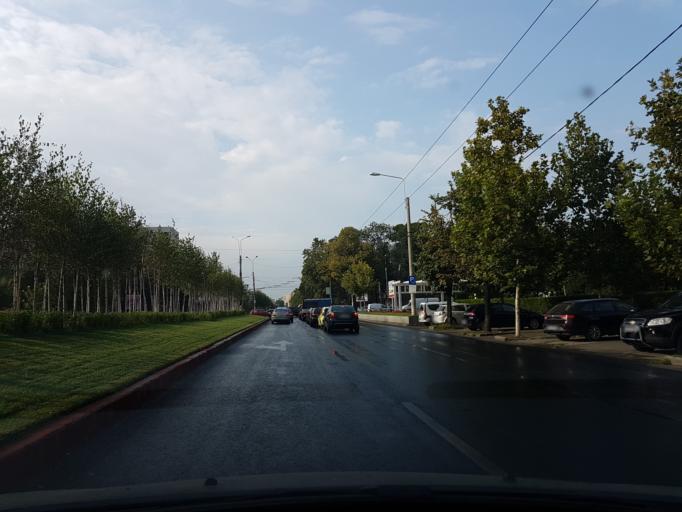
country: RO
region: Ilfov
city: Dobroesti
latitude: 44.4285
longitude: 26.1625
